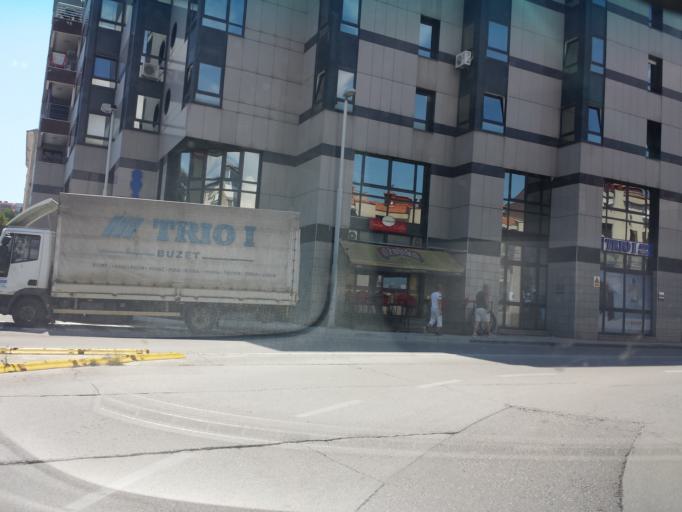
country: HR
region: Istarska
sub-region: Grad Pula
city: Pula
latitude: 44.8607
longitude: 13.8475
